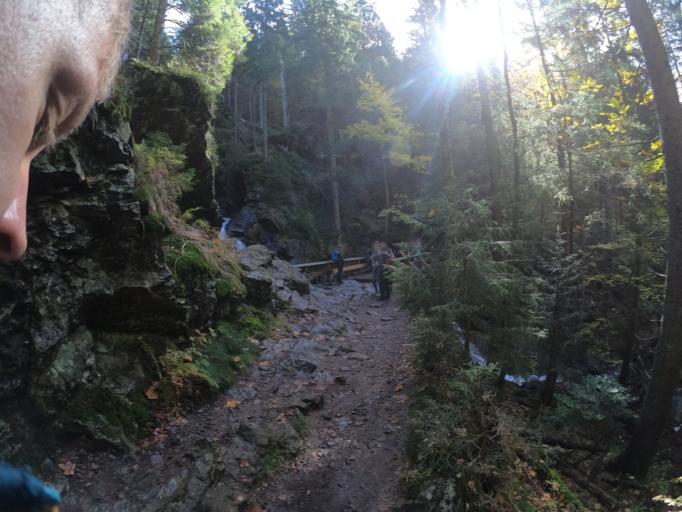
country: DE
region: Bavaria
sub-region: Lower Bavaria
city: Bodenmais
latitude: 49.0887
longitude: 13.1201
